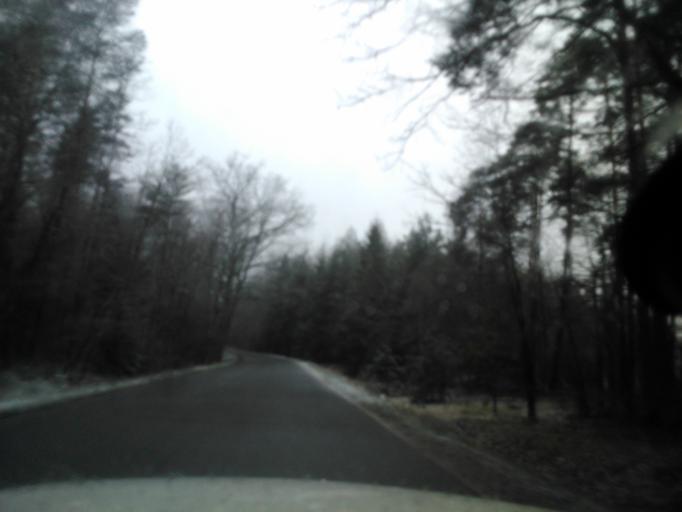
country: PL
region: Warmian-Masurian Voivodeship
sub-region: Powiat dzialdowski
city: Rybno
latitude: 53.3298
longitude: 19.9302
